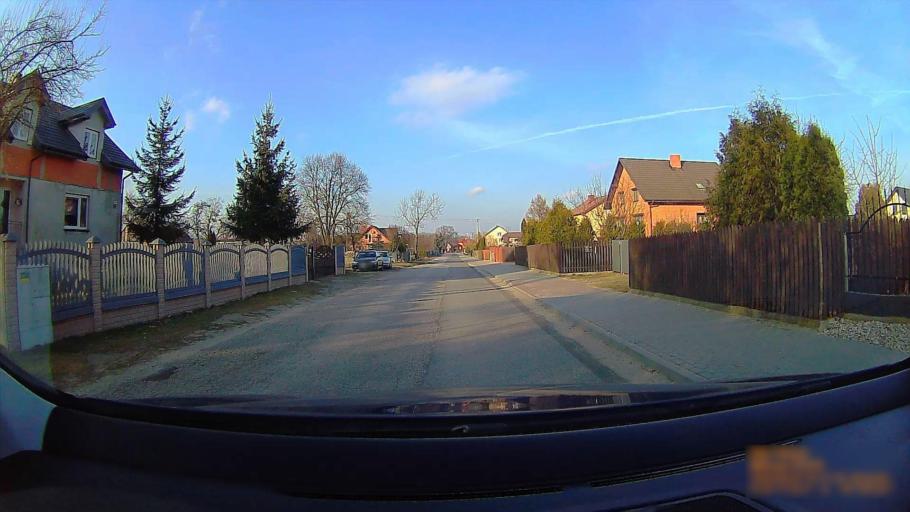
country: PL
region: Greater Poland Voivodeship
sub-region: Konin
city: Konin
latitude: 52.1864
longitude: 18.3016
